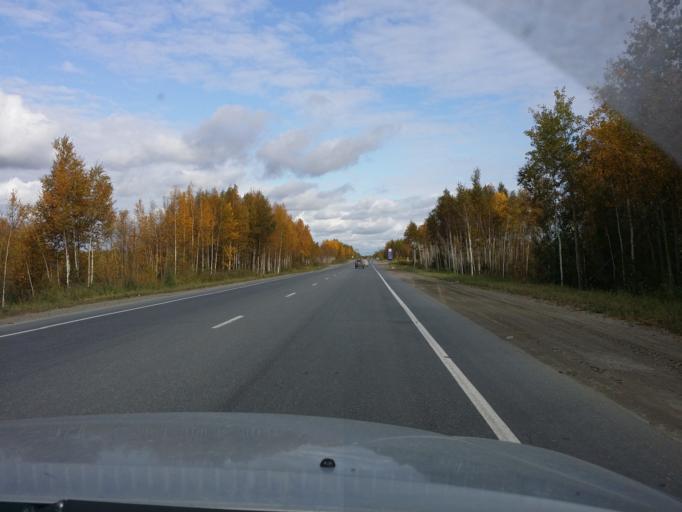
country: RU
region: Khanty-Mansiyskiy Avtonomnyy Okrug
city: Megion
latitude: 61.0670
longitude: 76.1157
